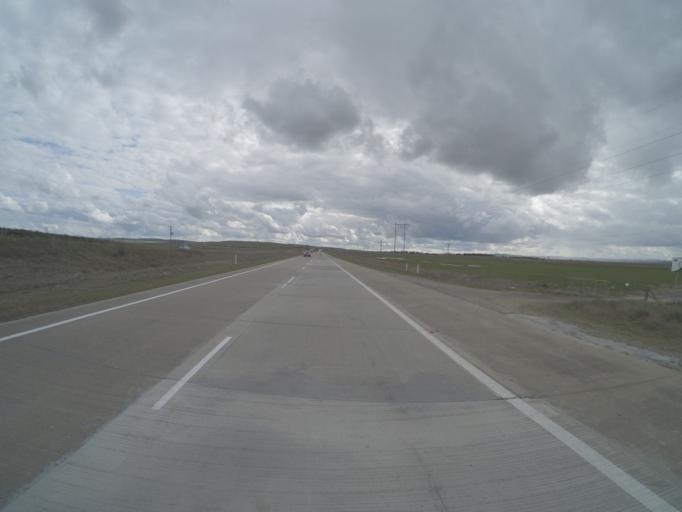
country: AU
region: New South Wales
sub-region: Goulburn Mulwaree
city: Goulburn
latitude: -34.8070
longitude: 149.5593
